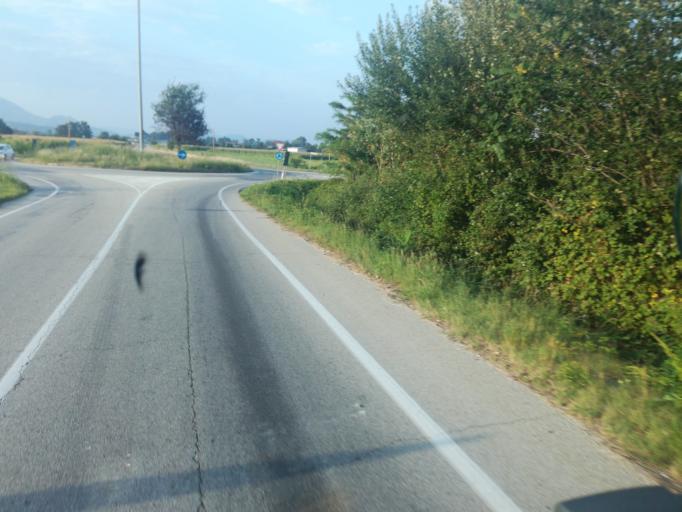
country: IT
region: Piedmont
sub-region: Provincia di Torino
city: Osasco
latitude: 44.8397
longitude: 7.3335
